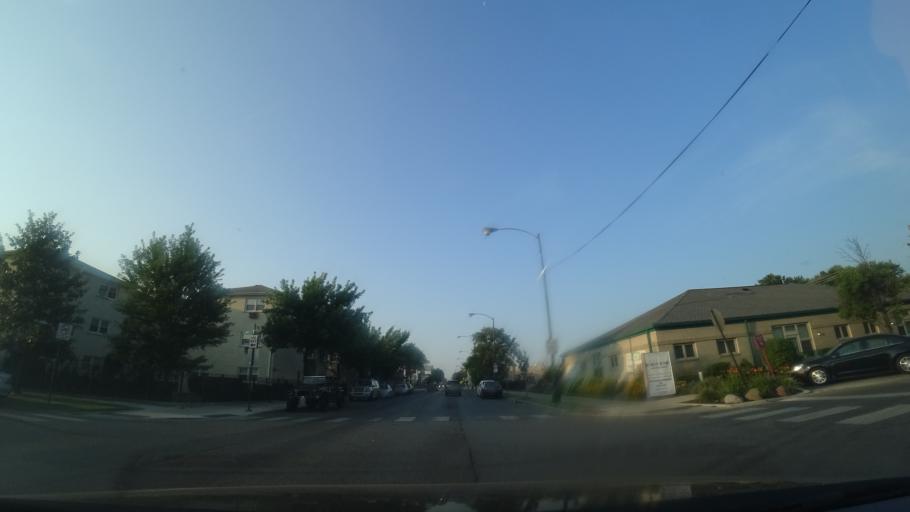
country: US
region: Illinois
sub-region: Cook County
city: Harwood Heights
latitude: 41.9451
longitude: -87.7668
